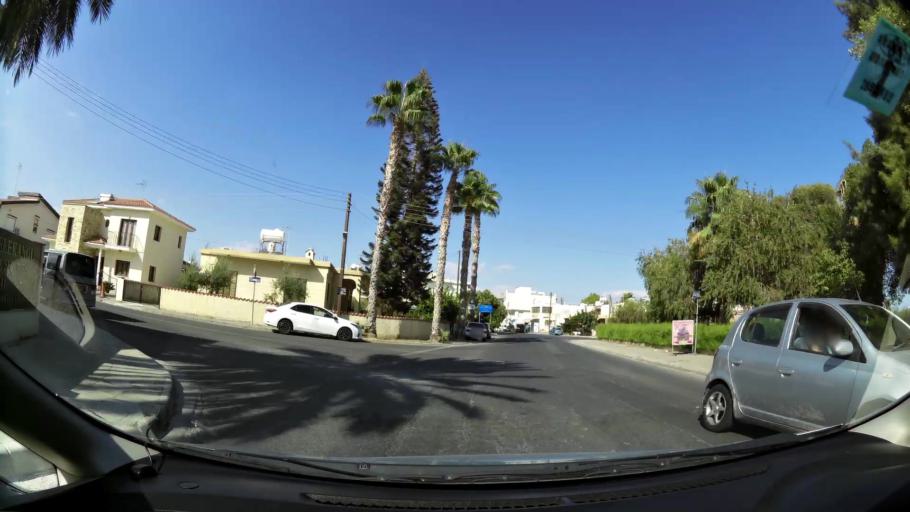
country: CY
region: Larnaka
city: Livadia
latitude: 34.9441
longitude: 33.6278
